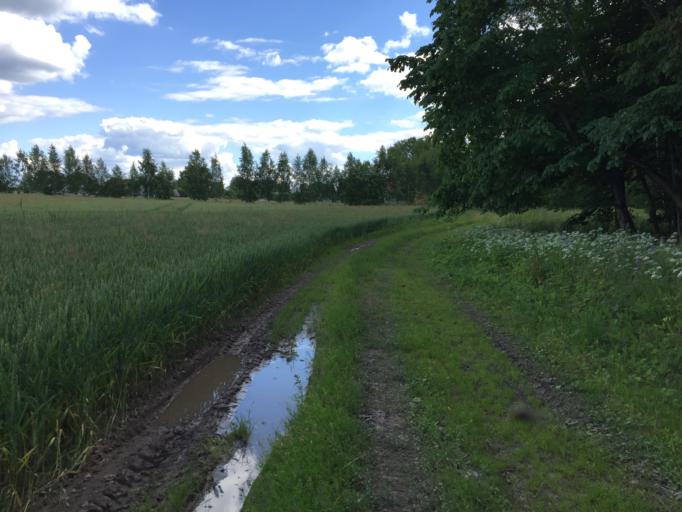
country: LV
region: Sigulda
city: Sigulda
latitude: 57.1698
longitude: 24.8820
